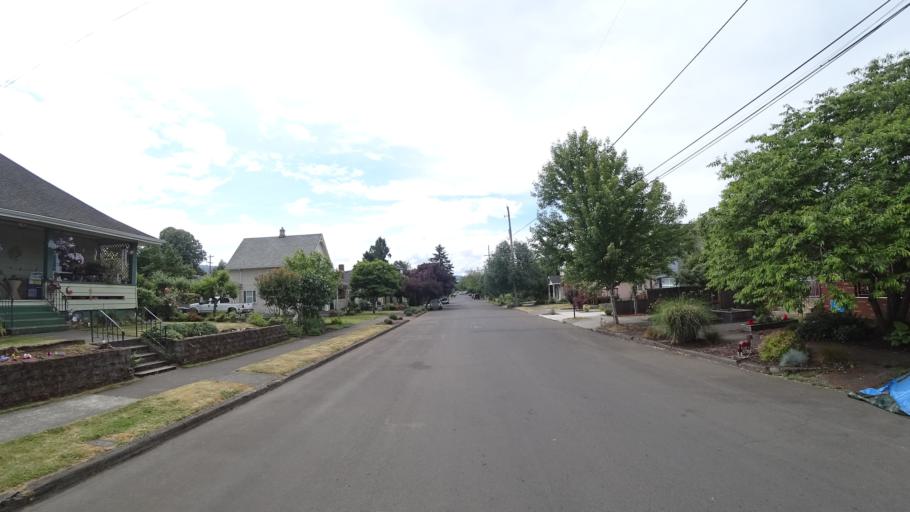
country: US
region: Oregon
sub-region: Washington County
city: West Haven
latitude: 45.5875
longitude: -122.7446
